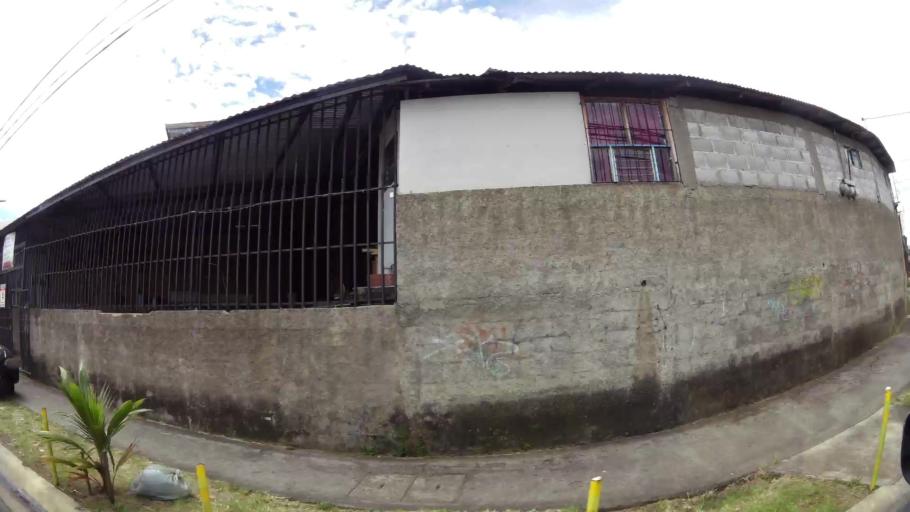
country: CR
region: San Jose
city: San Rafael Arriba
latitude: 9.8922
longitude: -84.0704
